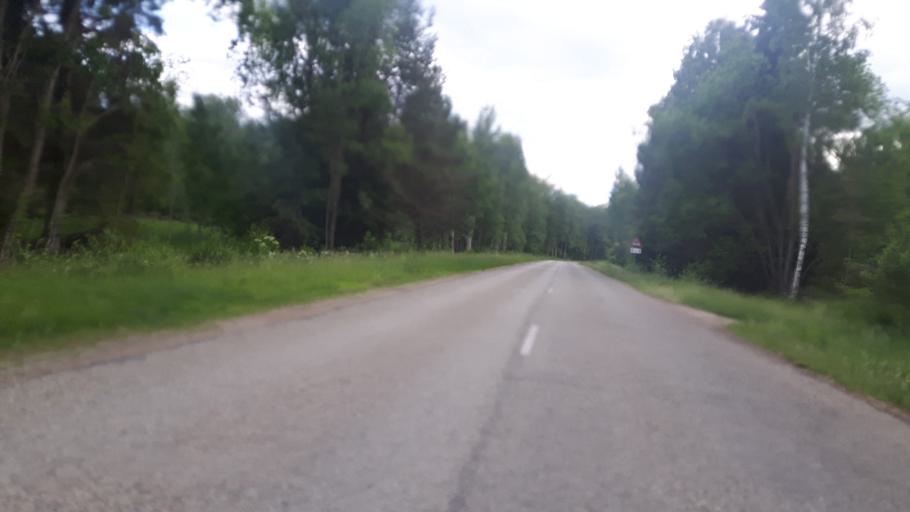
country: LV
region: Engure
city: Smarde
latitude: 57.0284
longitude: 23.3589
